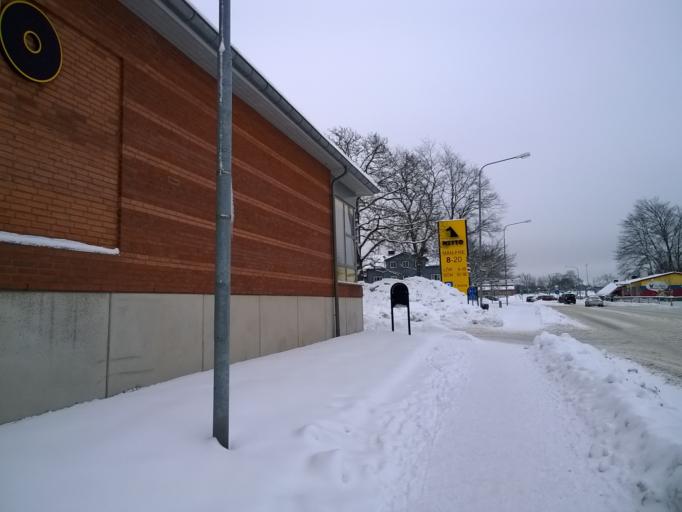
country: SE
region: Joenkoeping
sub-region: Nassjo Kommun
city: Nassjo
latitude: 57.6514
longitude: 14.6964
